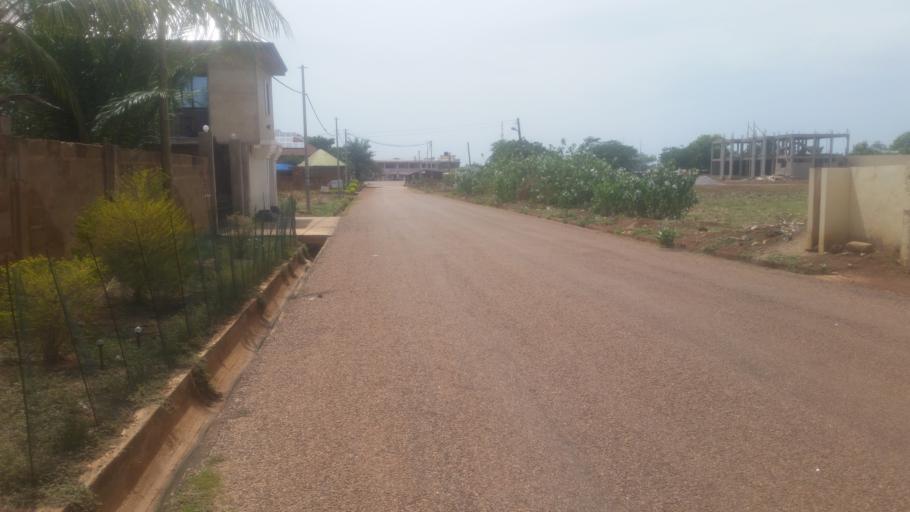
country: GH
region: Northern
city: Tamale
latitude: 9.4429
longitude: -0.8459
